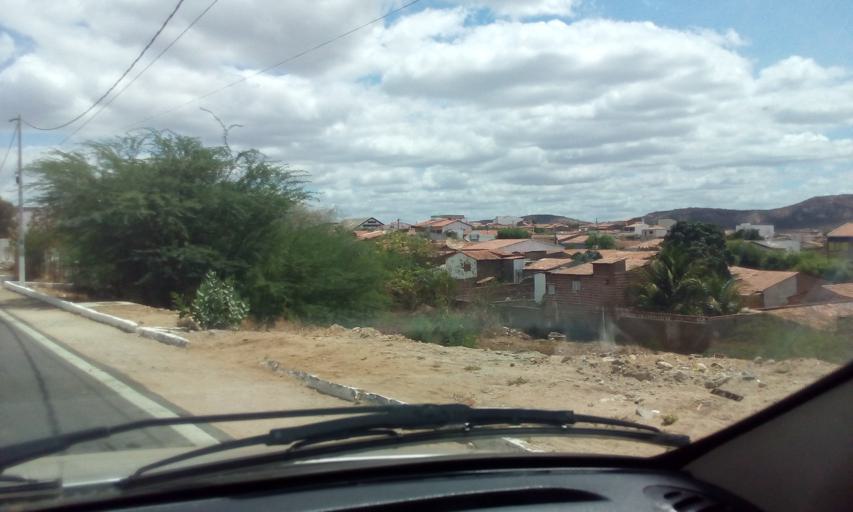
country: BR
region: Rio Grande do Norte
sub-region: Currais Novos
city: Currais Novos
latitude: -6.2679
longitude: -36.5220
